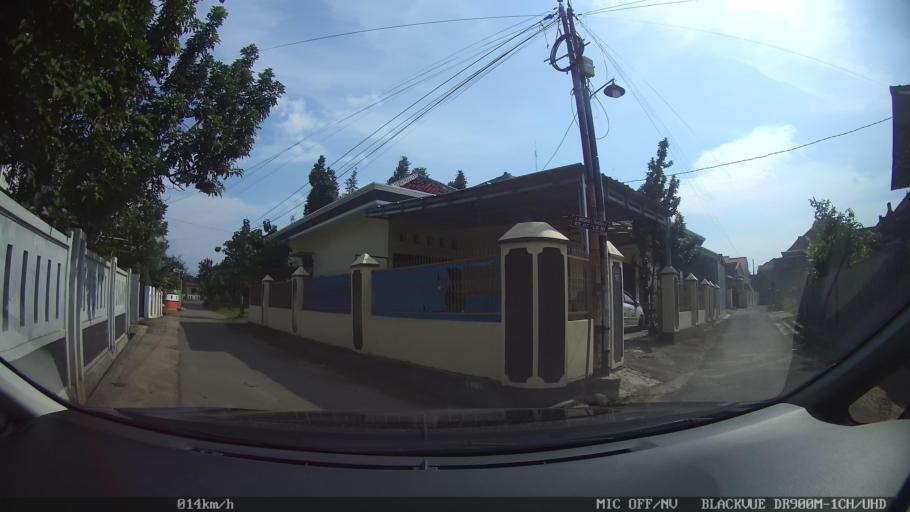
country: ID
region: Lampung
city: Kedaton
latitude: -5.3837
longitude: 105.2403
